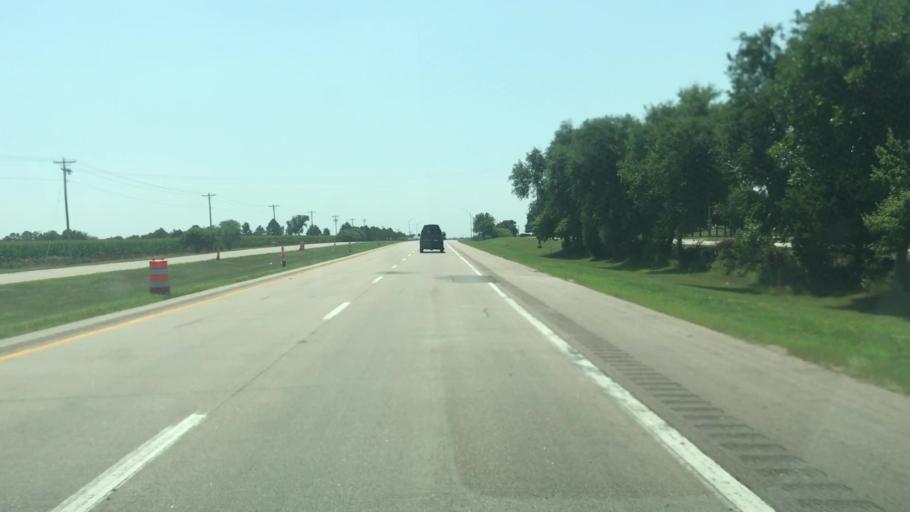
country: US
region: Nebraska
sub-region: Adams County
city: Hastings
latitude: 40.6373
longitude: -98.3820
